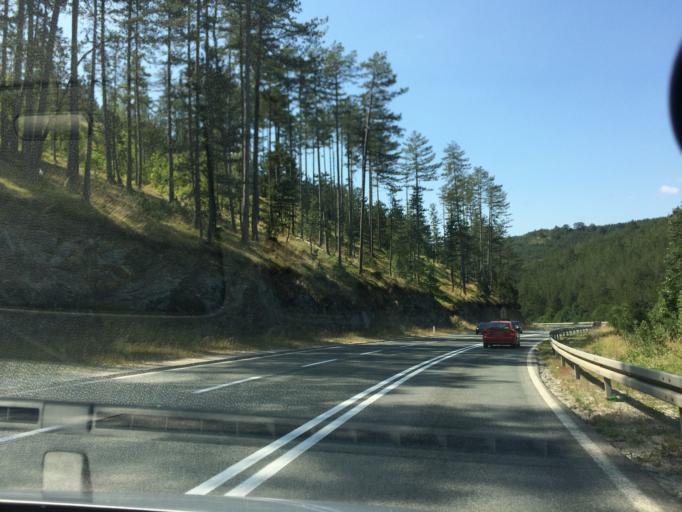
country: RS
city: Zlatibor
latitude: 43.6032
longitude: 19.7310
